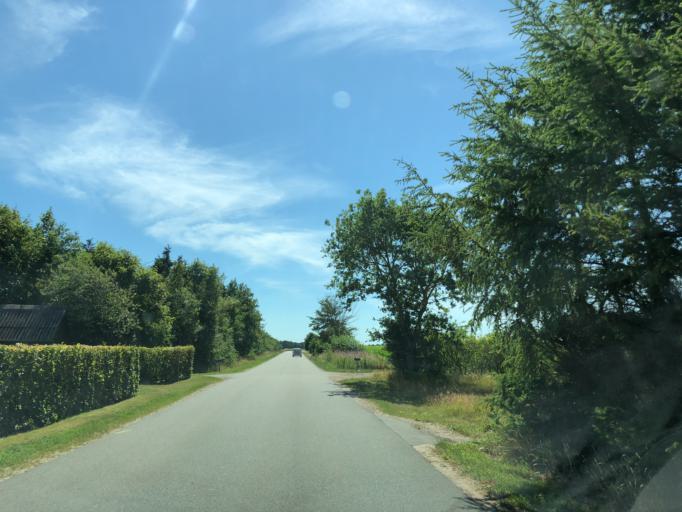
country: DK
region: Central Jutland
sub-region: Skive Kommune
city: Skive
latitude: 56.4376
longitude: 8.9595
